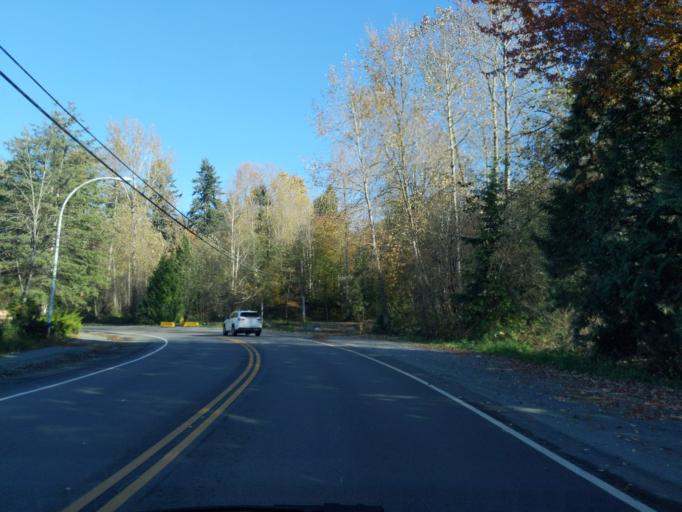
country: CA
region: British Columbia
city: New Westminster
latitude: 49.2027
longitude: -122.8690
